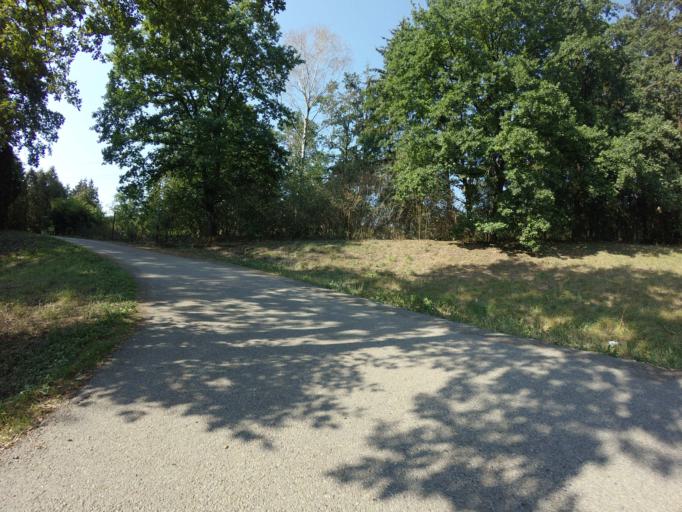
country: CZ
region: Central Bohemia
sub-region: Okres Benesov
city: Benesov
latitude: 49.7952
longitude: 14.6614
